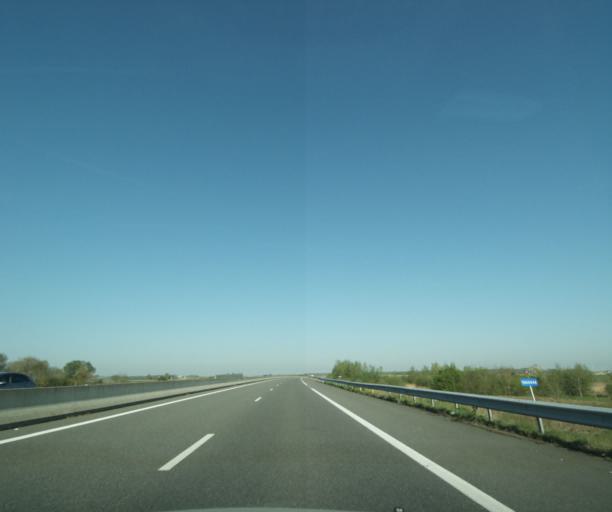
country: FR
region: Centre
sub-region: Departement du Loiret
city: Corbeilles
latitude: 48.0812
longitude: 2.6108
